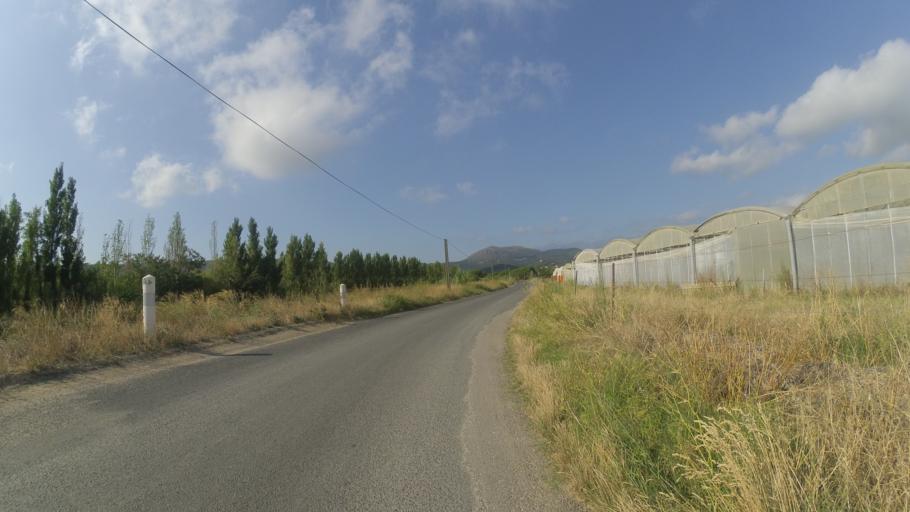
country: FR
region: Languedoc-Roussillon
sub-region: Departement des Pyrenees-Orientales
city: Millas
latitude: 42.6522
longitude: 2.7086
